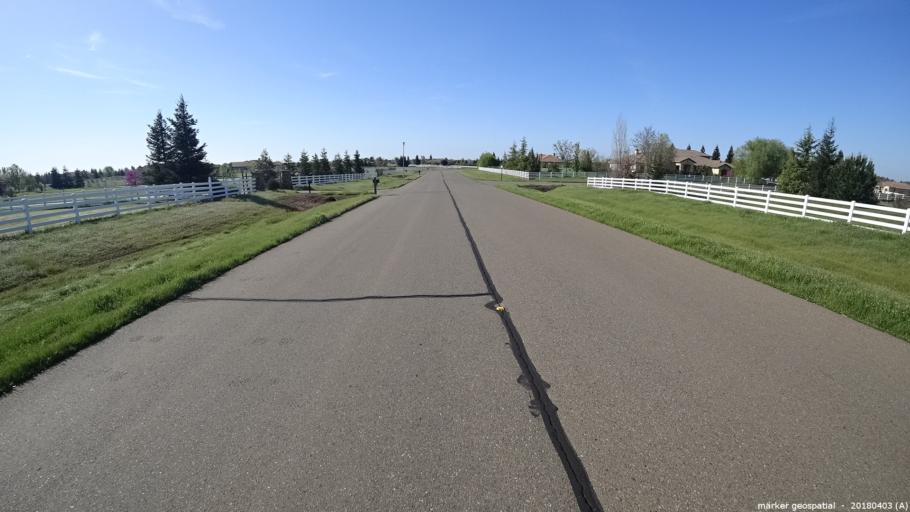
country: US
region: California
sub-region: Sacramento County
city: Wilton
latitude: 38.4178
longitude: -121.1982
